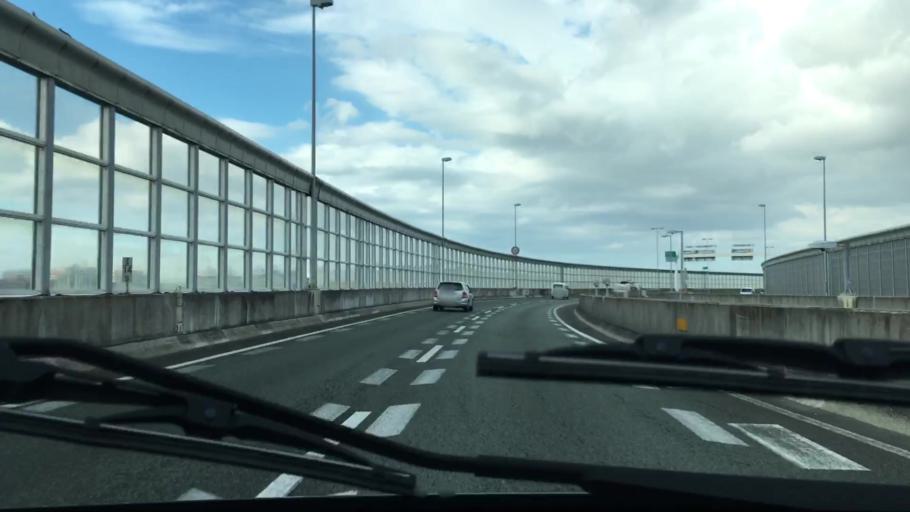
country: JP
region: Fukuoka
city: Fukuoka-shi
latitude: 33.5861
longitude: 130.3407
